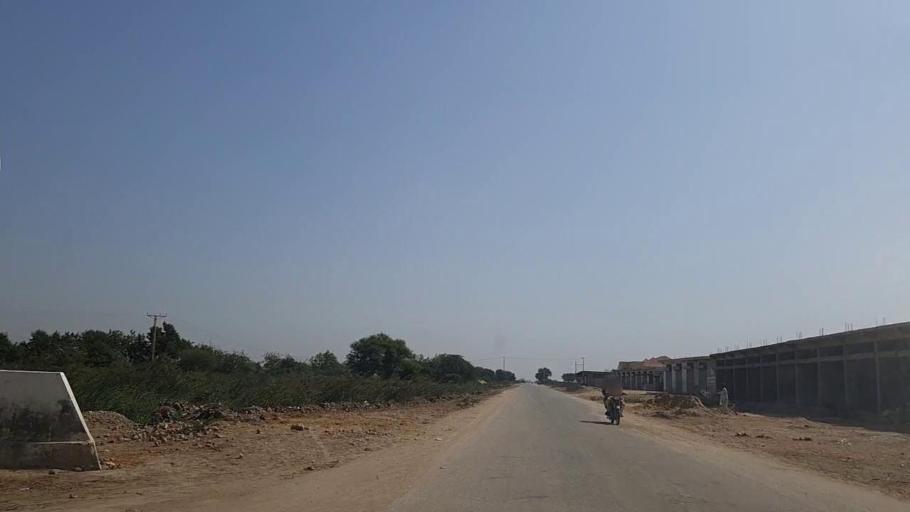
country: PK
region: Sindh
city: Daro Mehar
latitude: 24.7922
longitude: 68.1851
